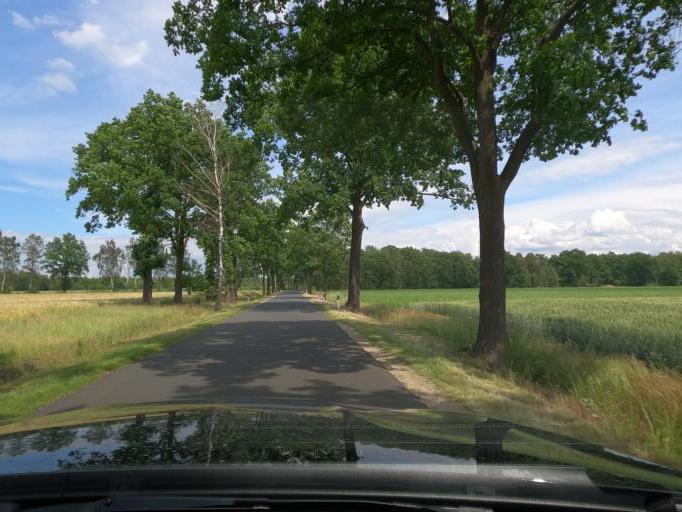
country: DE
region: Lower Saxony
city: Lindwedel
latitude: 52.6106
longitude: 9.6280
